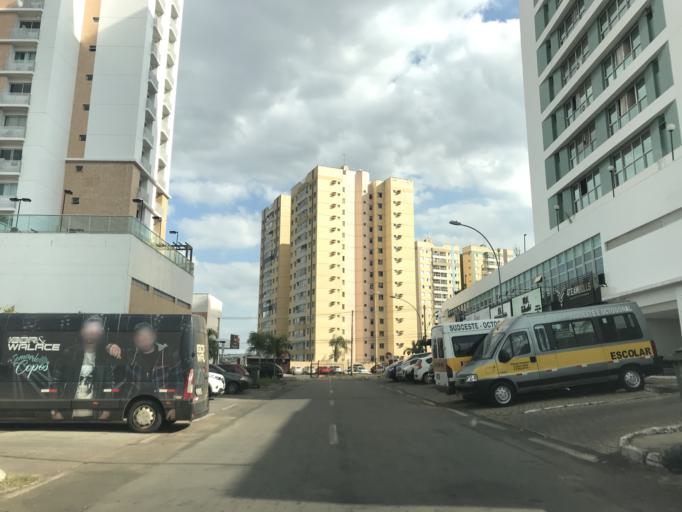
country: BR
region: Federal District
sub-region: Brasilia
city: Brasilia
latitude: -15.8367
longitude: -48.0096
